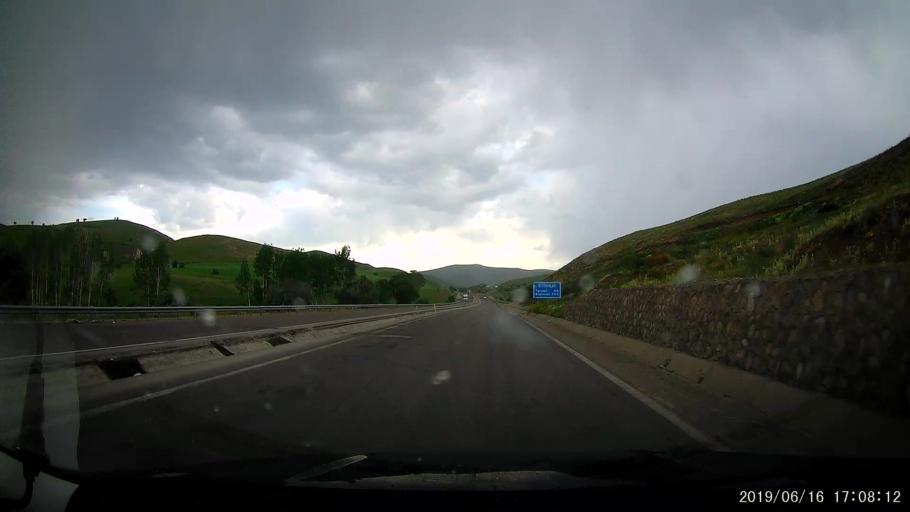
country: TR
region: Erzurum
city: Askale
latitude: 39.9123
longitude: 40.6639
